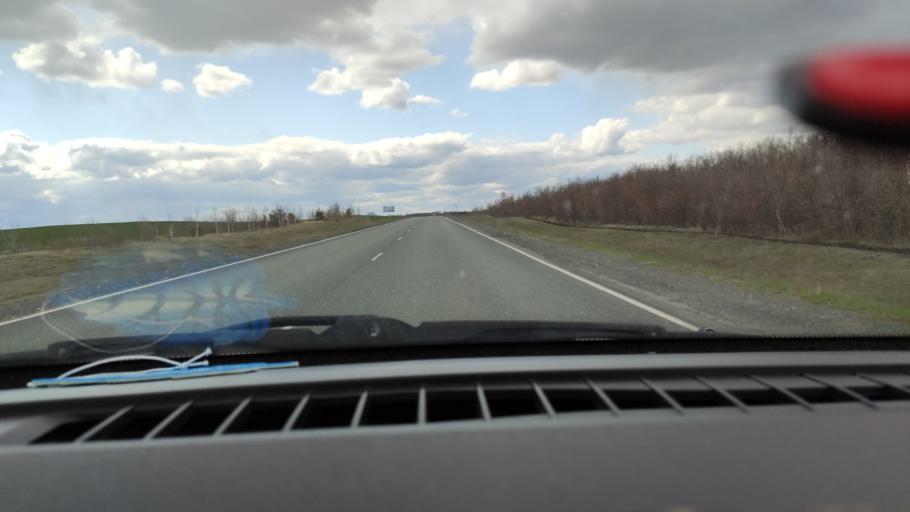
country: RU
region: Saratov
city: Balakovo
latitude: 52.1774
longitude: 47.8379
